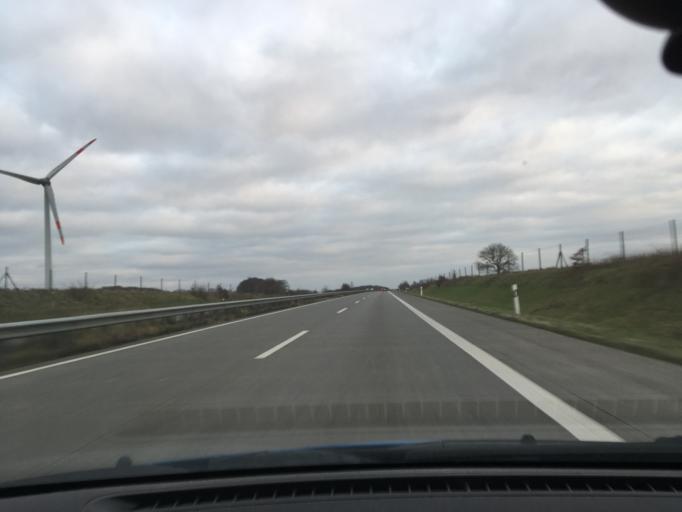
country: DE
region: Schleswig-Holstein
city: Nienbuttel
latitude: 54.0432
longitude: 9.4121
